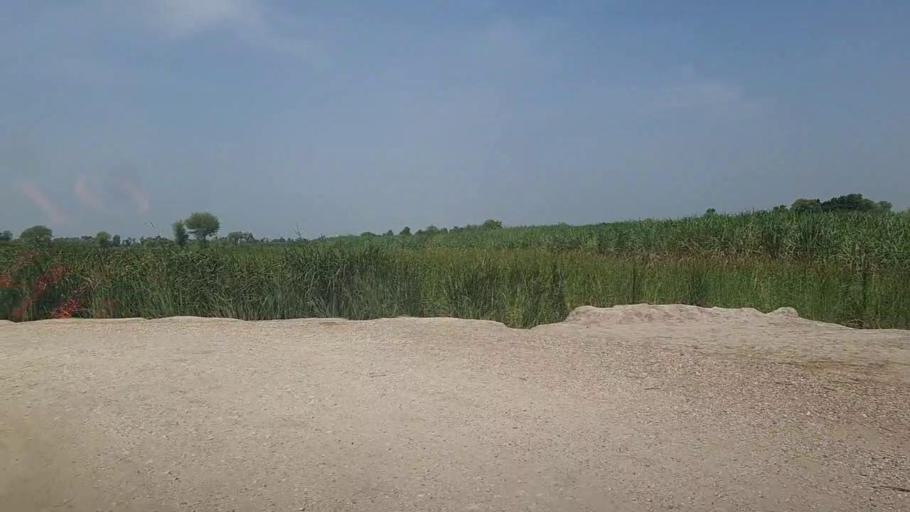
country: PK
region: Sindh
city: Ubauro
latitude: 28.1602
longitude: 69.8280
